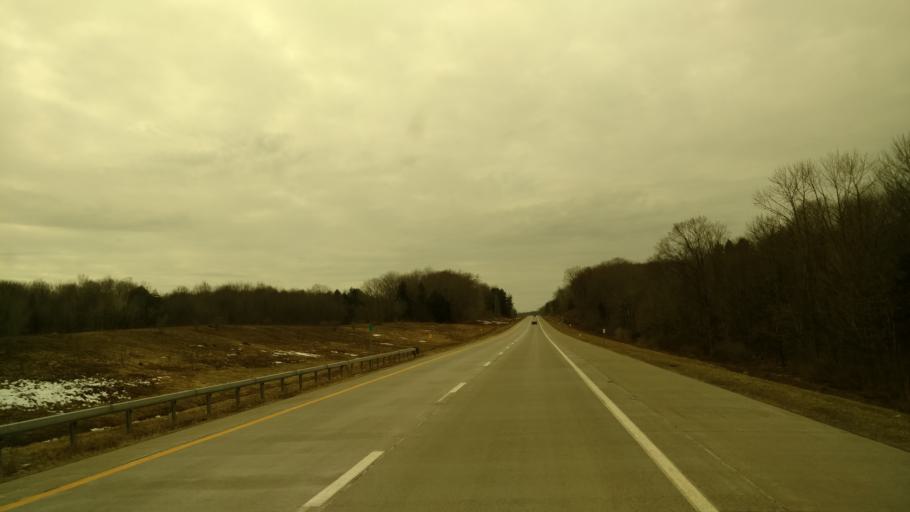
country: US
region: New York
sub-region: Chautauqua County
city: Mayville
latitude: 42.1551
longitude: -79.4524
